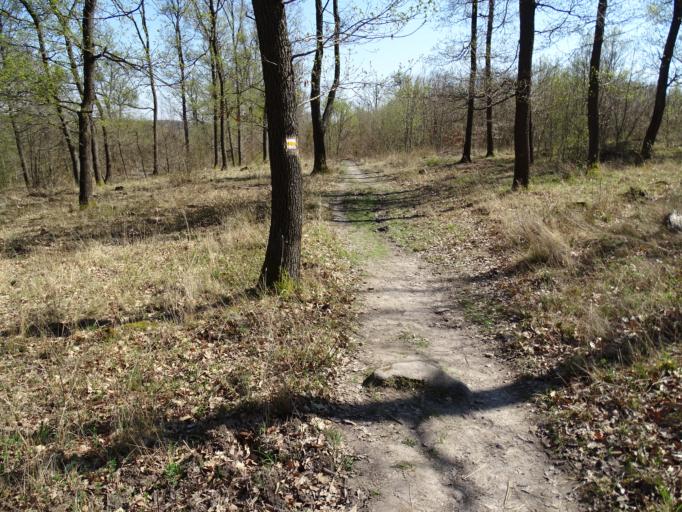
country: HU
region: Pest
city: Nagykovacsi
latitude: 47.6854
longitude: 18.9946
